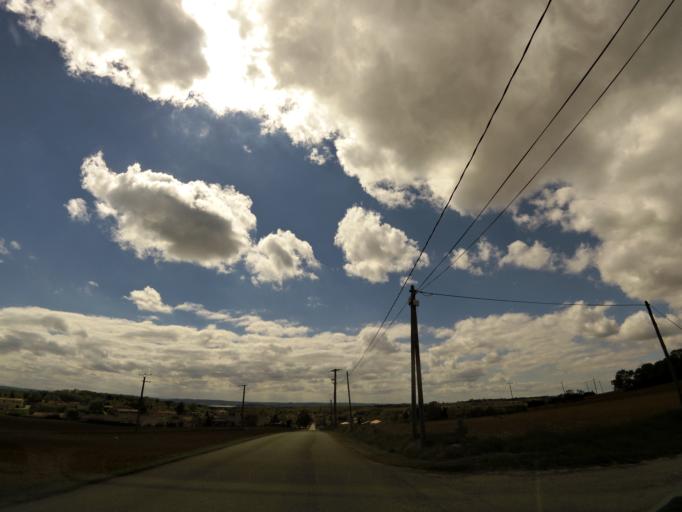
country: FR
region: Languedoc-Roussillon
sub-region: Departement de l'Aude
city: Saint-Martin-Lalande
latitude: 43.3334
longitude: 2.0447
